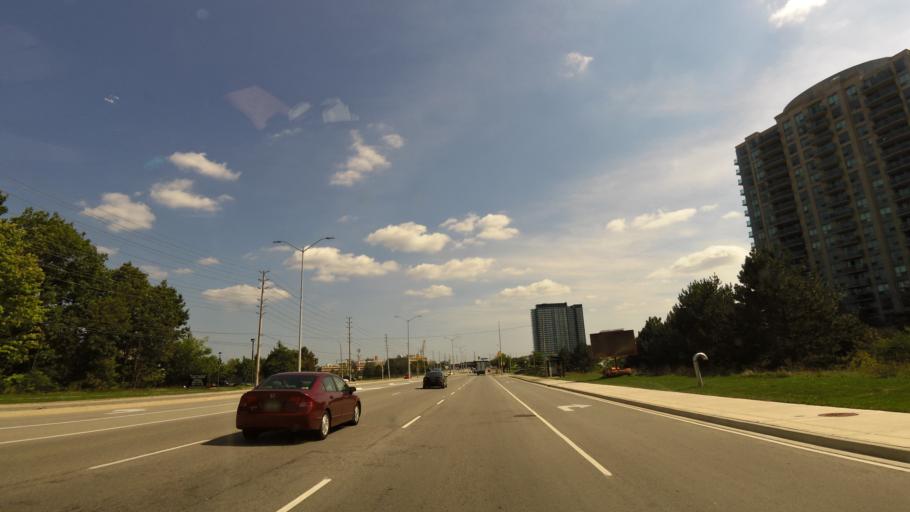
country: CA
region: Ontario
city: Mississauga
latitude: 43.5627
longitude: -79.7123
